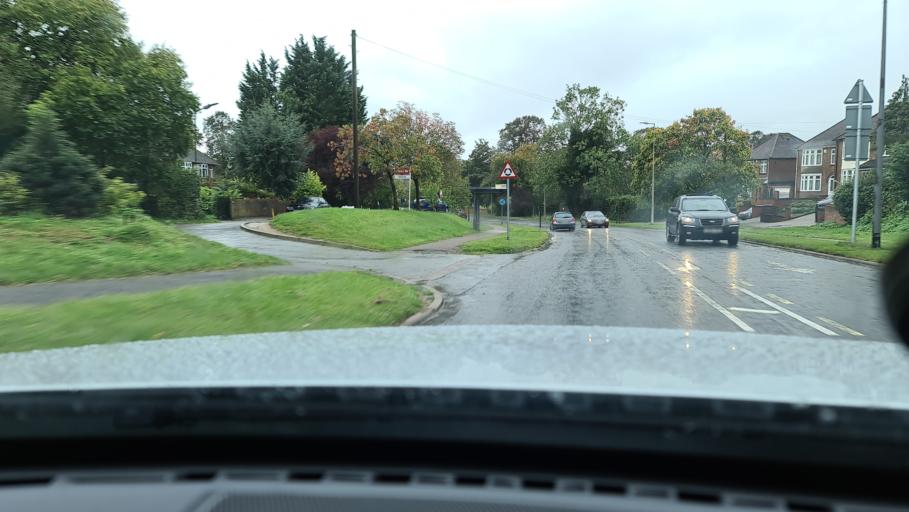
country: GB
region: England
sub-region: Milton Keynes
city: Water Eaton
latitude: 51.9922
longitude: -0.7203
